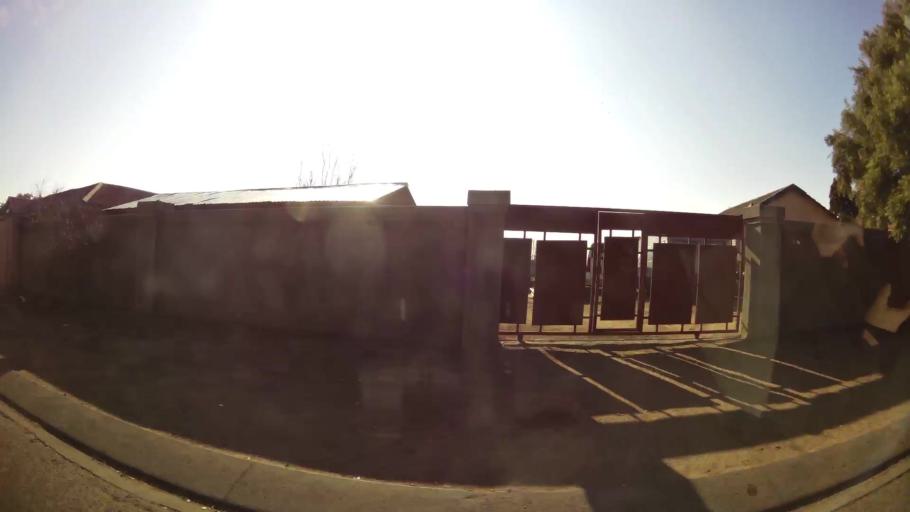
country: ZA
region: Orange Free State
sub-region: Mangaung Metropolitan Municipality
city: Bloemfontein
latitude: -29.1860
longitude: 26.1741
